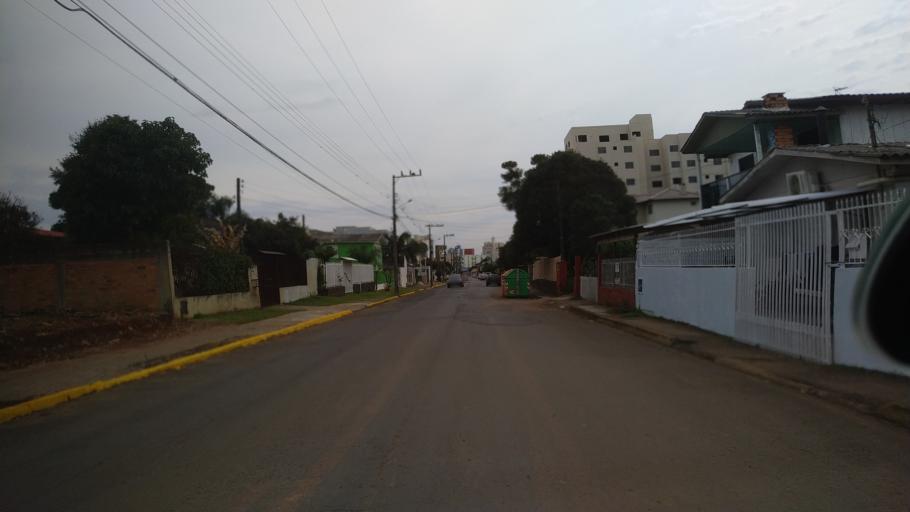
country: BR
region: Santa Catarina
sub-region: Chapeco
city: Chapeco
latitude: -27.1134
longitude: -52.6021
